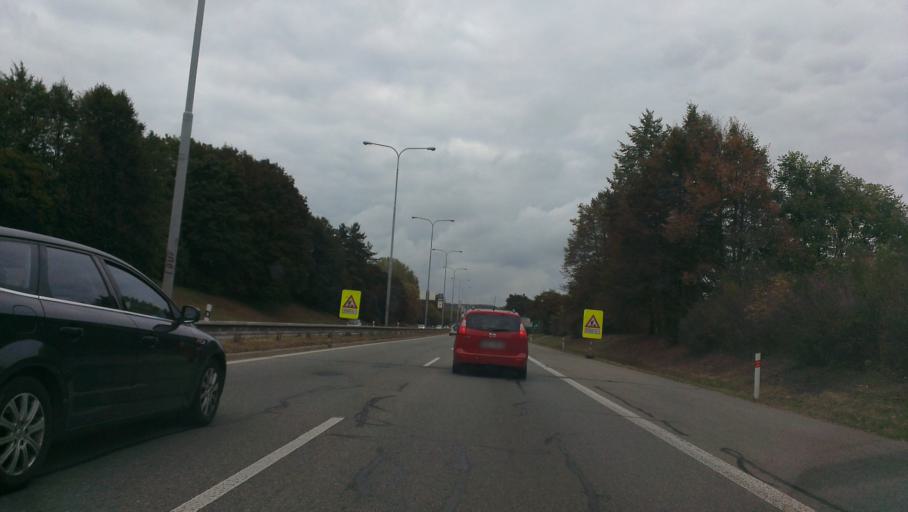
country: CZ
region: South Moravian
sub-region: Mesto Brno
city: Mokra Hora
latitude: 49.2442
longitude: 16.5892
